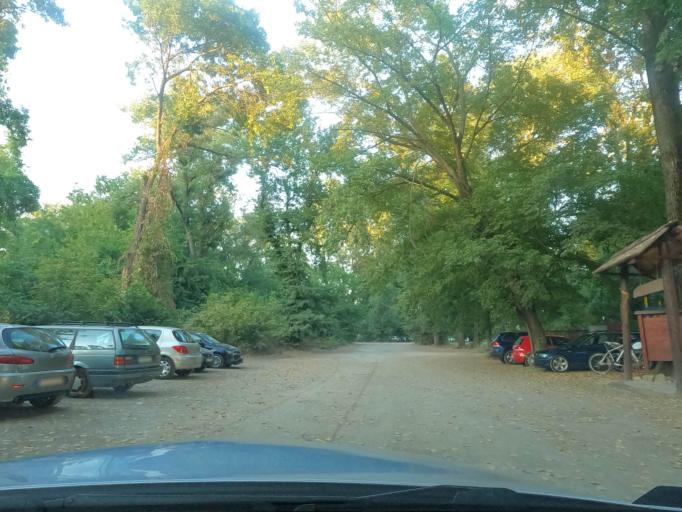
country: RS
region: Autonomna Pokrajina Vojvodina
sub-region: Juznobacki Okrug
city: Novi Sad
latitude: 45.2318
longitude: 19.8395
